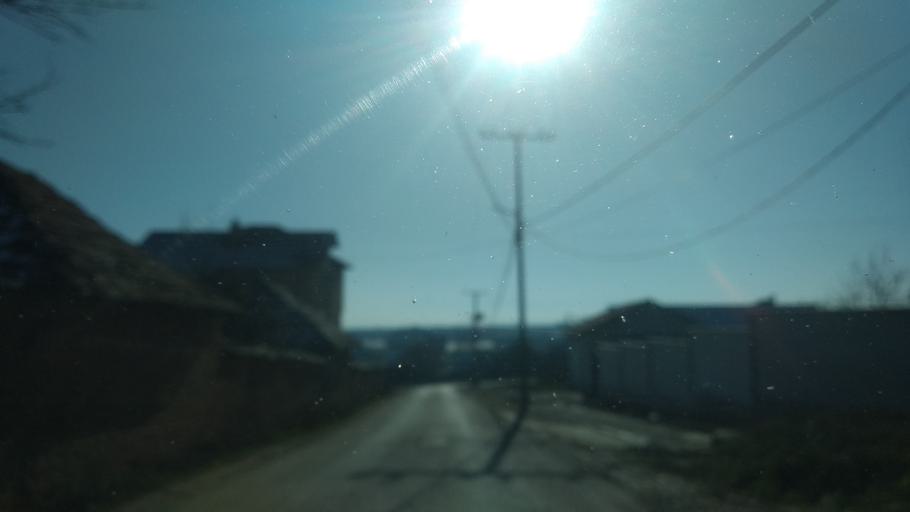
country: XK
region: Pristina
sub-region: Komuna e Gracanices
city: Glanica
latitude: 42.6061
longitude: 21.0282
